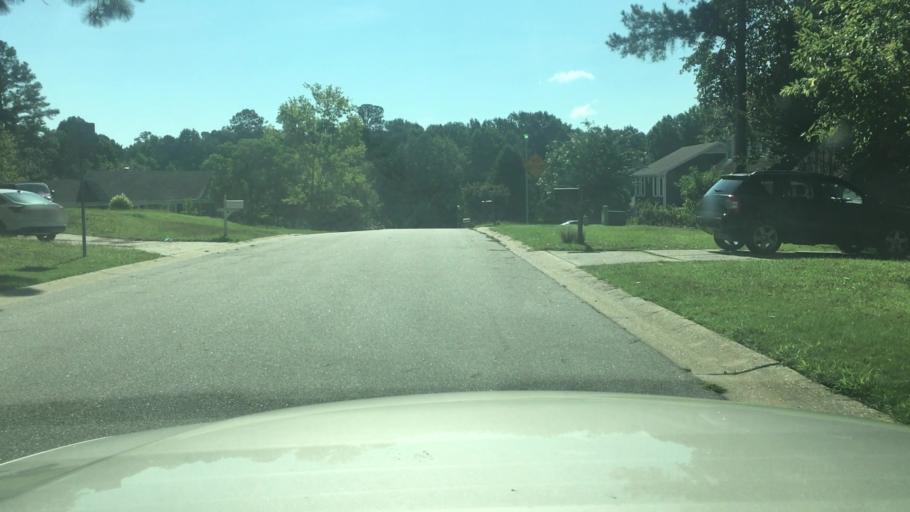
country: US
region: North Carolina
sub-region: Cumberland County
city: Fayetteville
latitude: 35.1145
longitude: -78.8976
